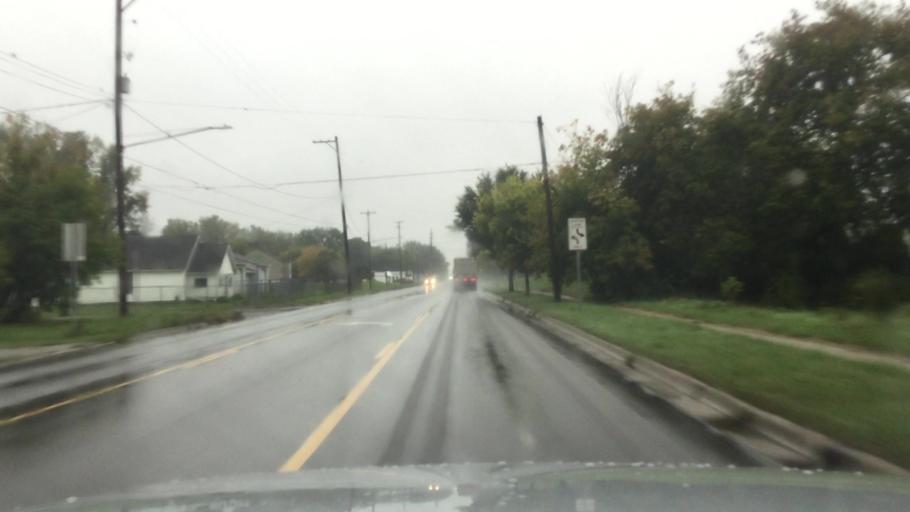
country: US
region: Michigan
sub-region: Saginaw County
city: Saginaw
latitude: 43.3908
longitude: -83.9555
